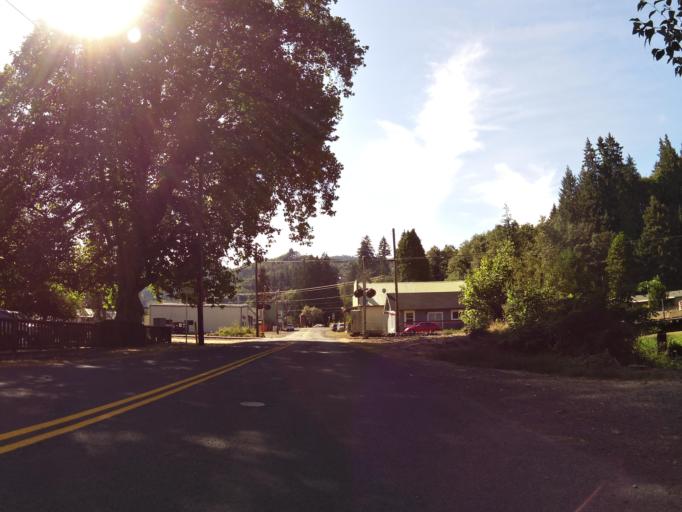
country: US
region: Washington
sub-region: Wahkiakum County
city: Cathlamet
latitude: 46.1335
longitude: -123.3761
